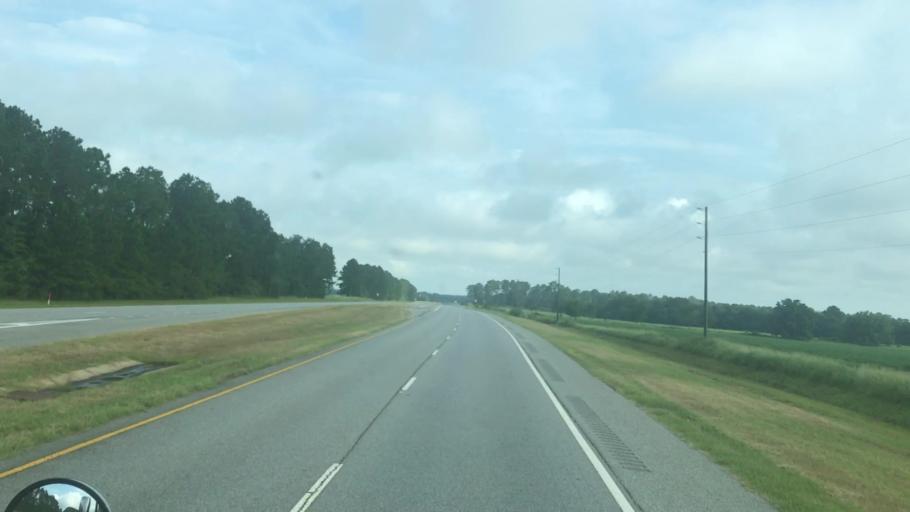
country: US
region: Georgia
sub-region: Miller County
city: Colquitt
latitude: 31.2063
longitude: -84.7720
